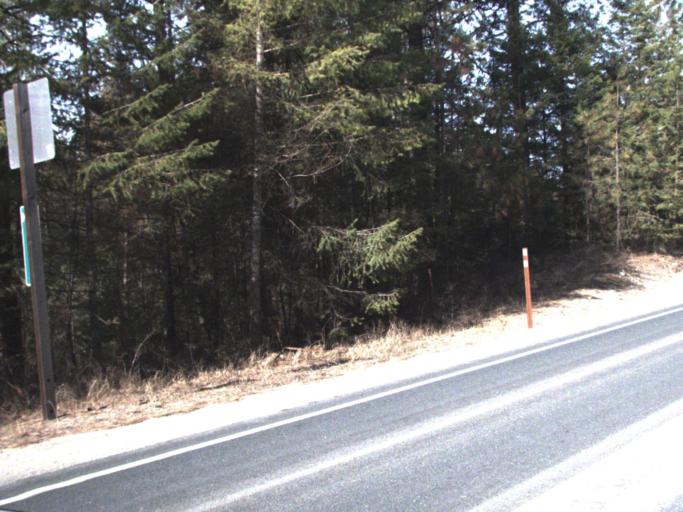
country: US
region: Washington
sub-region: Stevens County
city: Colville
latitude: 48.5031
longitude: -117.7152
